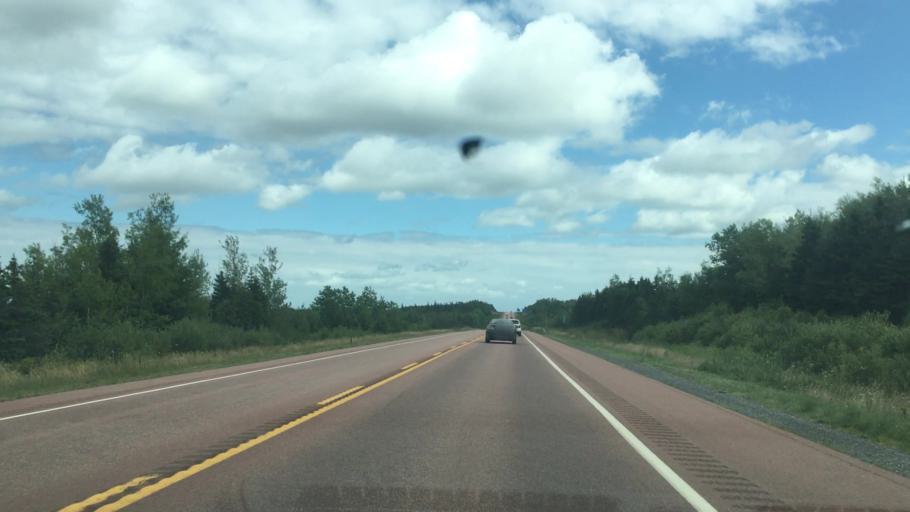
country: CA
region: Nova Scotia
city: Antigonish
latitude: 45.6043
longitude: -61.6861
